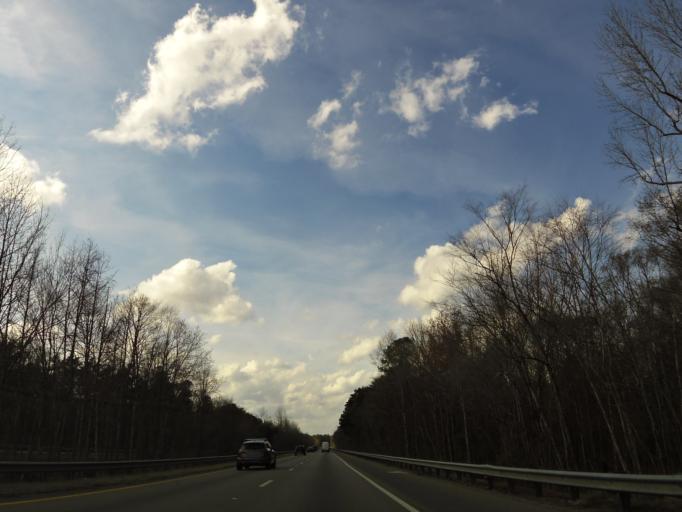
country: US
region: South Carolina
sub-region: Dorchester County
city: Ridgeville
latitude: 33.1488
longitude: -80.3342
